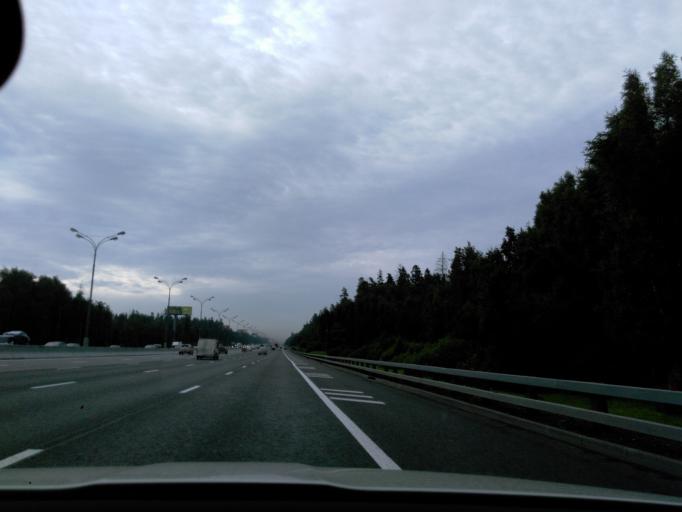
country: RU
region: Moscow
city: Metrogorodok
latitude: 55.8545
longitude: 37.7799
